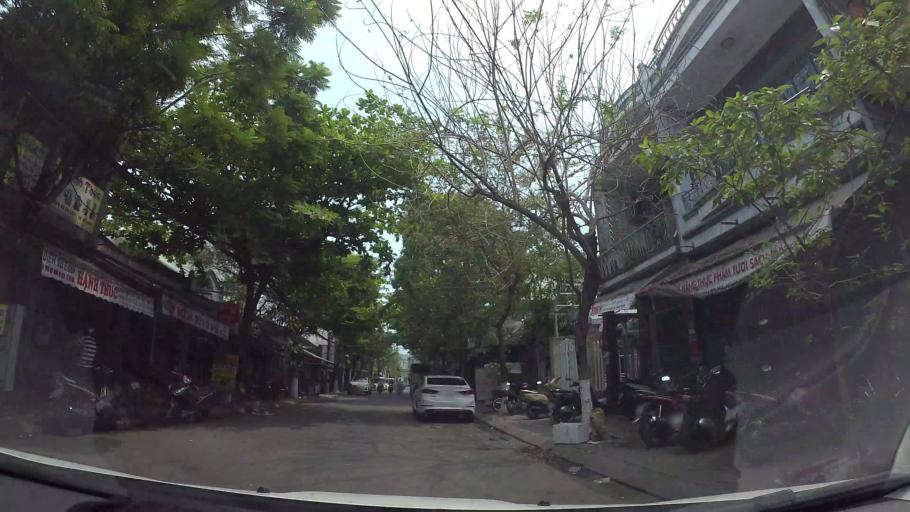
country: VN
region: Da Nang
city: Son Tra
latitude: 16.1004
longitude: 108.2529
